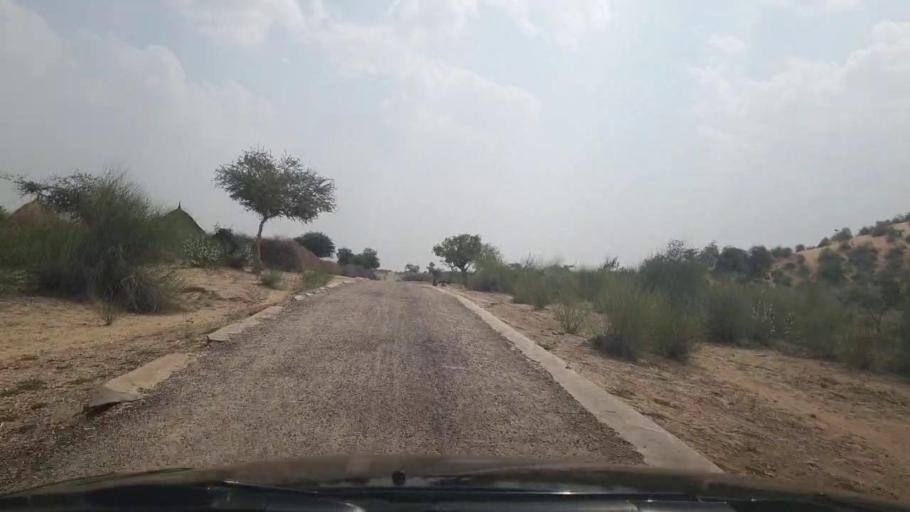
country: PK
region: Sindh
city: Islamkot
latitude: 25.0118
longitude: 70.5268
